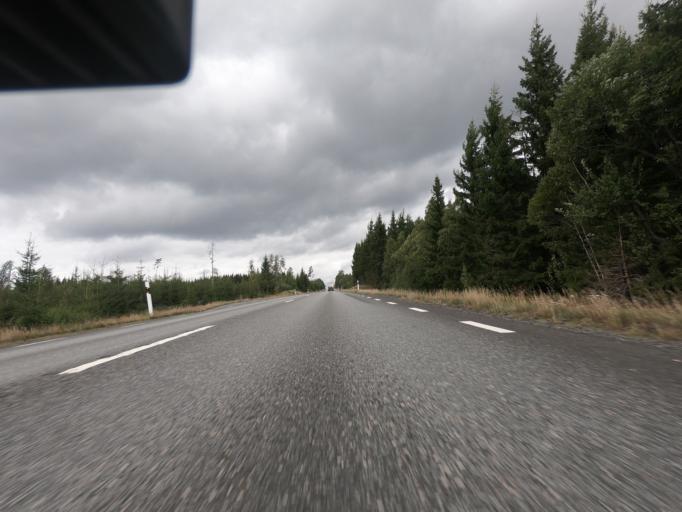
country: SE
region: Joenkoeping
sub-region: Savsjo Kommun
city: Vrigstad
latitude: 57.4149
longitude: 14.3393
